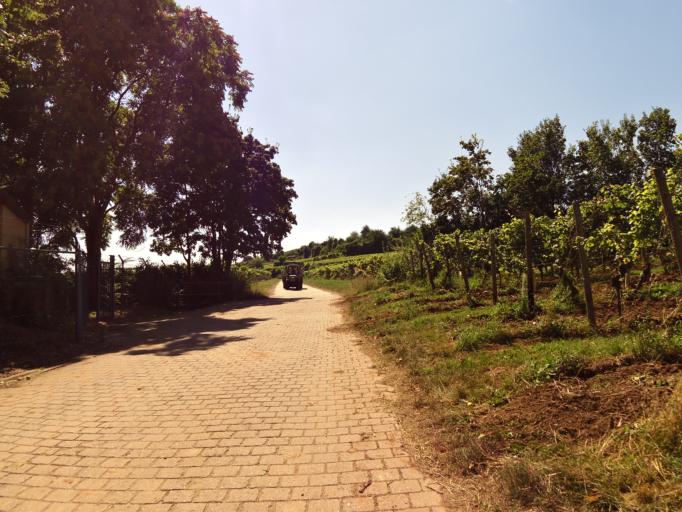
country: DE
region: Rheinland-Pfalz
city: Nierstein
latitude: 49.8834
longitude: 8.3370
